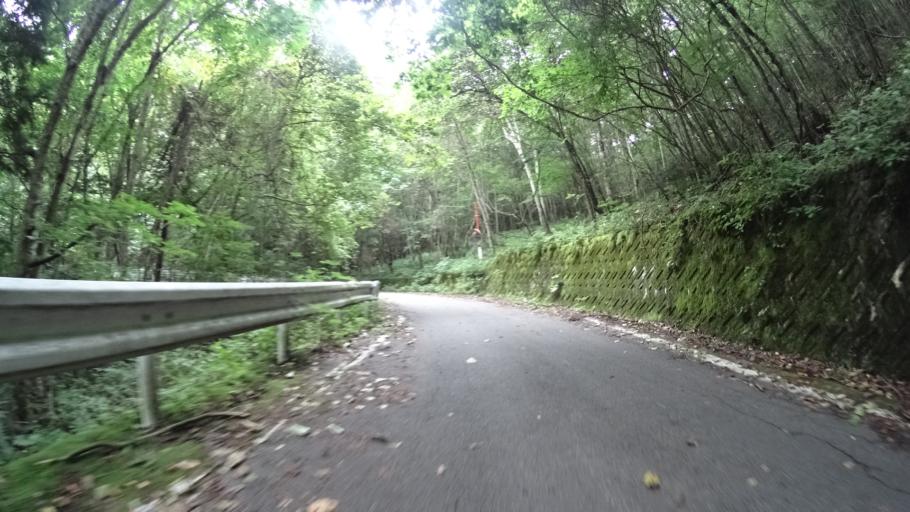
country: JP
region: Yamanashi
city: Kofu-shi
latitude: 35.8054
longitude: 138.6184
